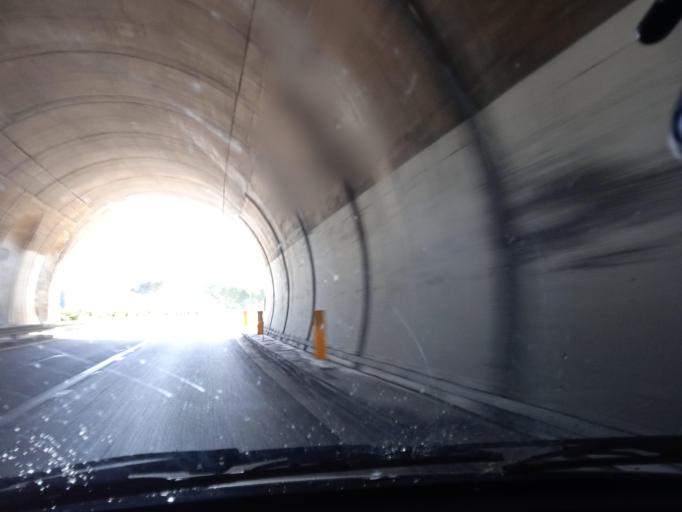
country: IT
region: Sicily
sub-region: Messina
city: Naso
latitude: 38.1506
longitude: 14.7685
